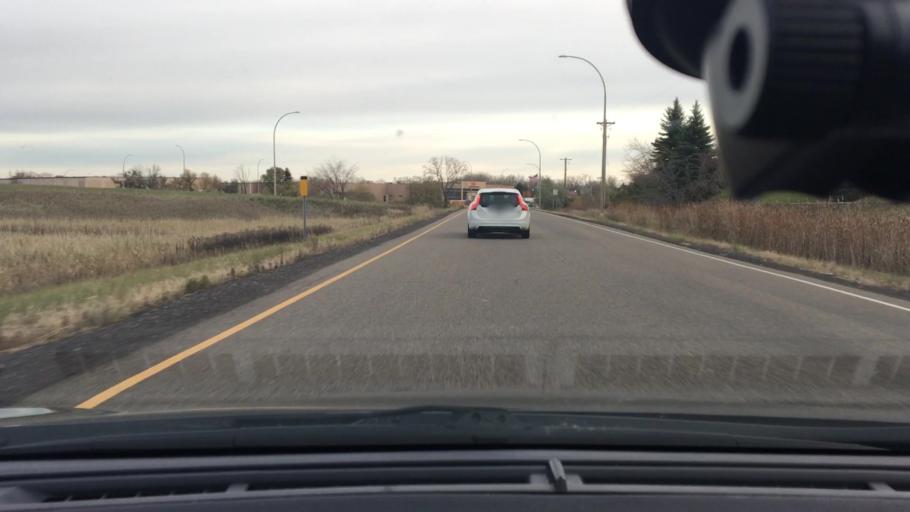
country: US
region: Minnesota
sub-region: Hennepin County
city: New Hope
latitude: 45.0577
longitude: -93.4034
